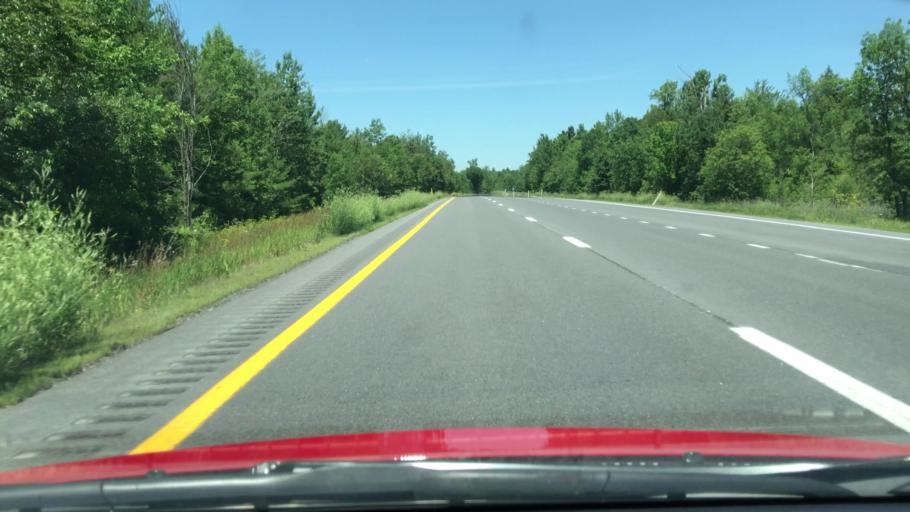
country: US
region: New York
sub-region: Clinton County
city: Champlain
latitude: 44.8922
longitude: -73.4537
